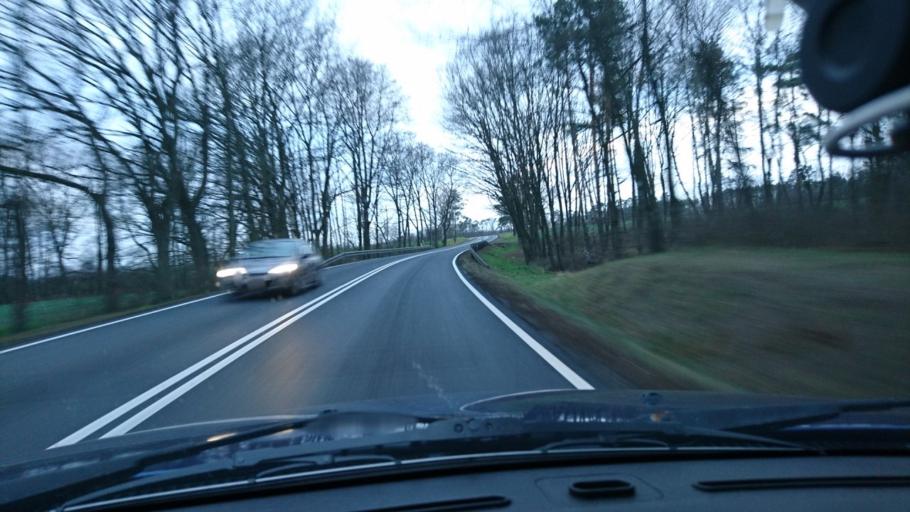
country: PL
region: Opole Voivodeship
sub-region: Powiat kluczborski
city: Byczyna
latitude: 51.1487
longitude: 18.1861
